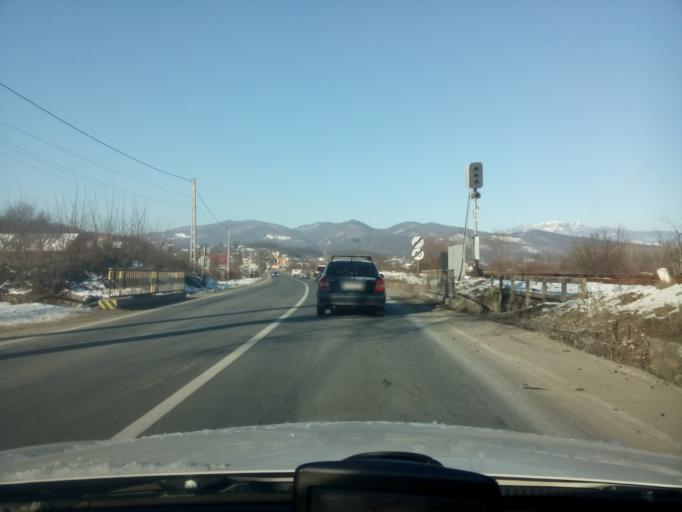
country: RO
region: Valcea
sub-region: Comuna Bujoreni
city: Bujoreni
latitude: 45.1642
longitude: 24.3706
